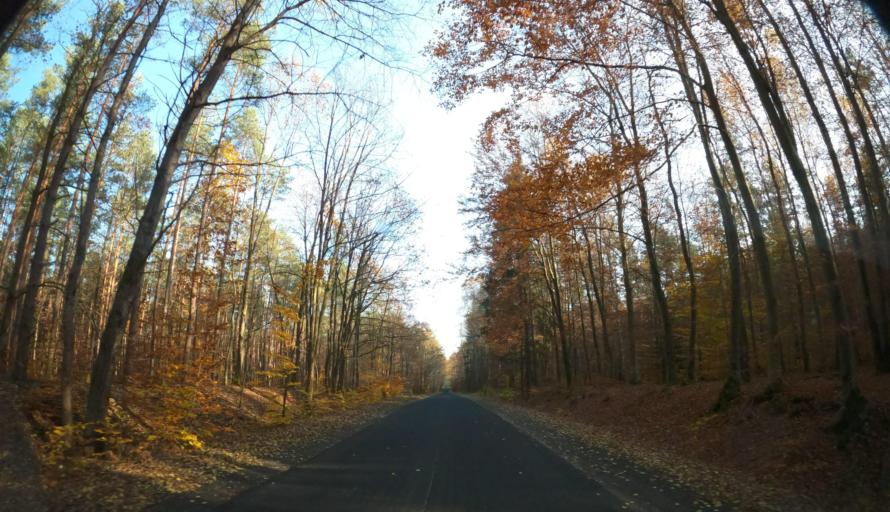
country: PL
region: West Pomeranian Voivodeship
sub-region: Powiat koszalinski
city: Polanow
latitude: 54.2410
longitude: 16.7158
